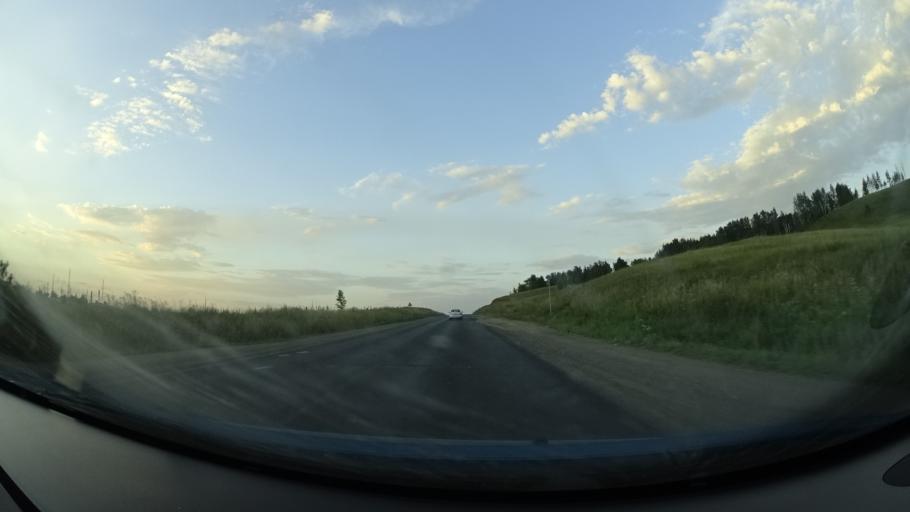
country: RU
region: Orenburg
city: Severnoye
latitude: 54.1697
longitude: 52.6438
